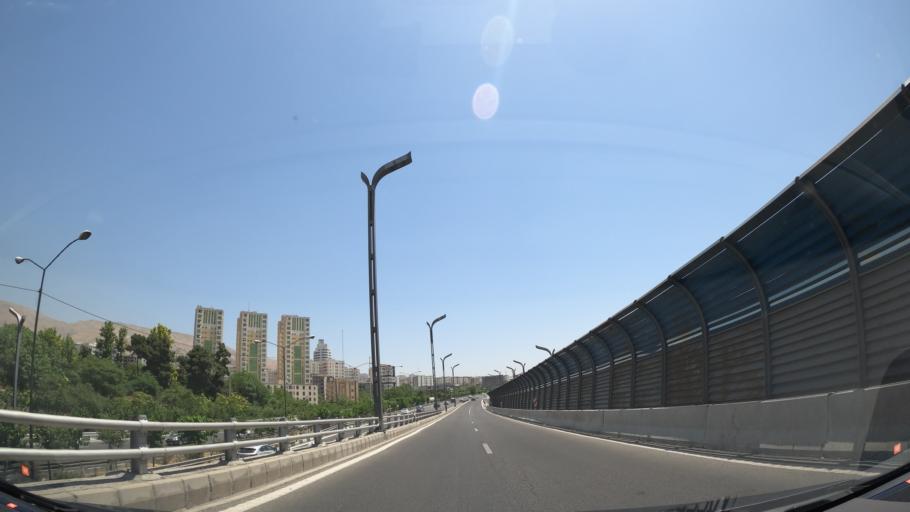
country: IR
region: Tehran
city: Tajrish
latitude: 35.7858
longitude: 51.4957
